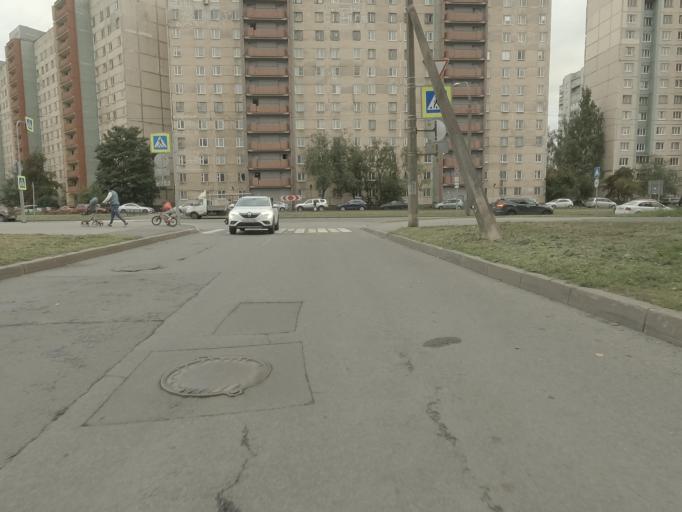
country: RU
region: St.-Petersburg
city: Krasnogvargeisky
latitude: 59.9557
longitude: 30.4870
